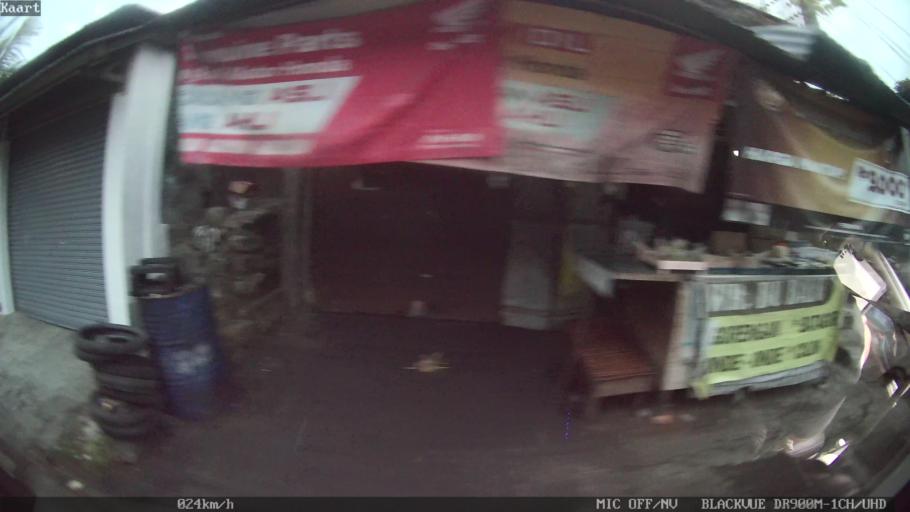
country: ID
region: Bali
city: Banjar Kertajiwa
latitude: -8.6329
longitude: 115.2605
